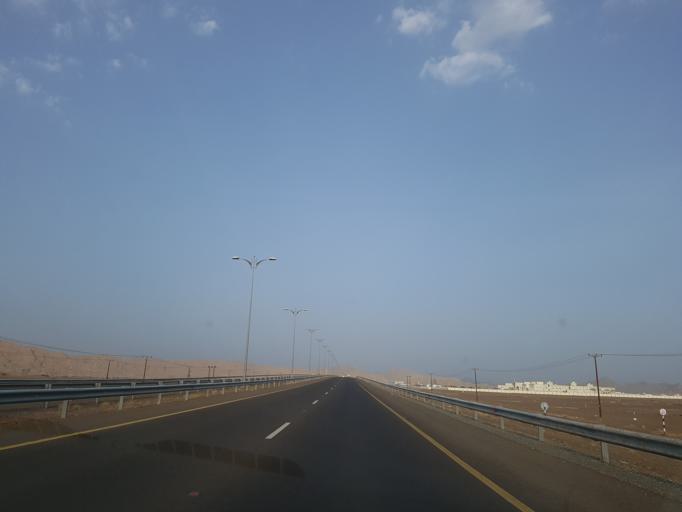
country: OM
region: Al Buraimi
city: Al Buraymi
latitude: 24.2376
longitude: 55.9028
